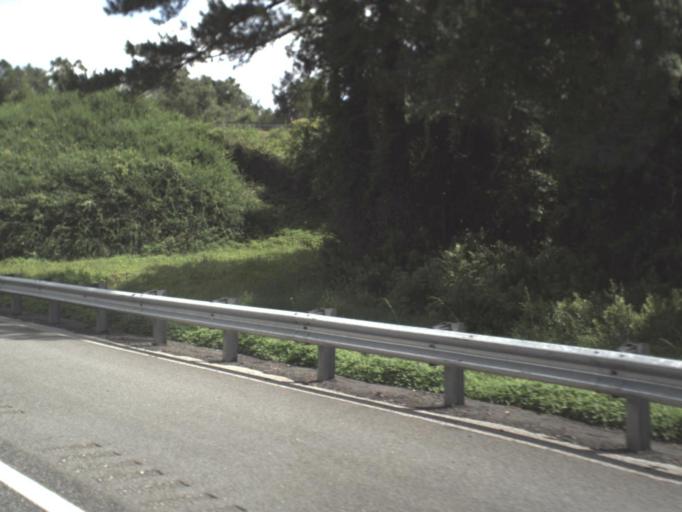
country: US
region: Florida
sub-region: Alachua County
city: High Springs
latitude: 29.9516
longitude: -82.5685
